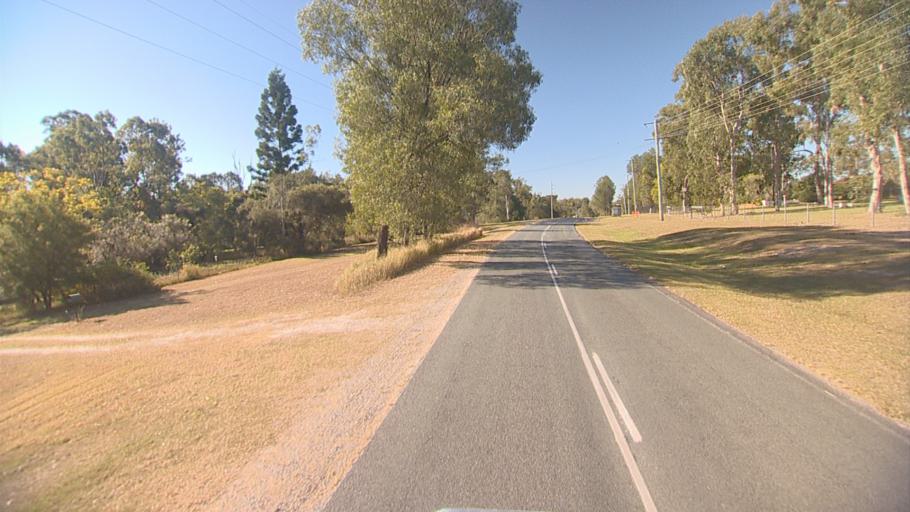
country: AU
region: Queensland
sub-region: Logan
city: North Maclean
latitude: -27.7883
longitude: 153.0443
